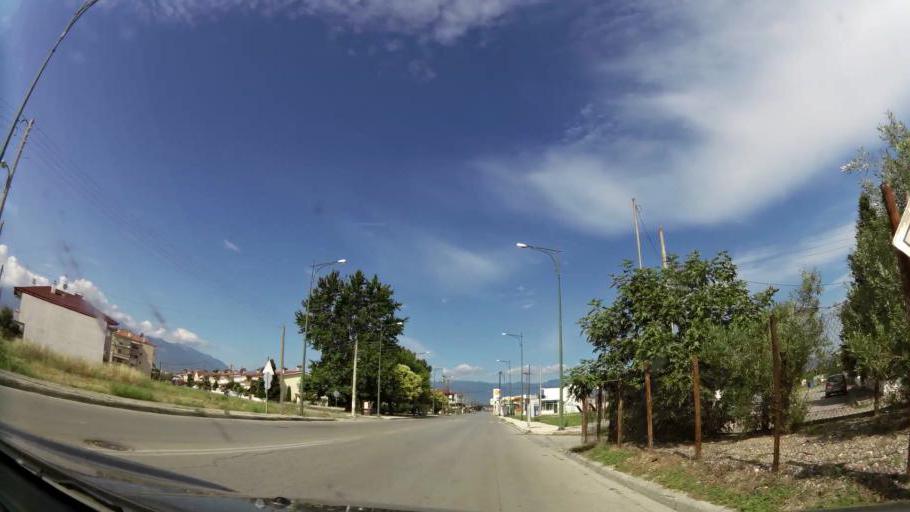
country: GR
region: Central Macedonia
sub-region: Nomos Pierias
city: Katerini
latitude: 40.2843
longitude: 22.5171
